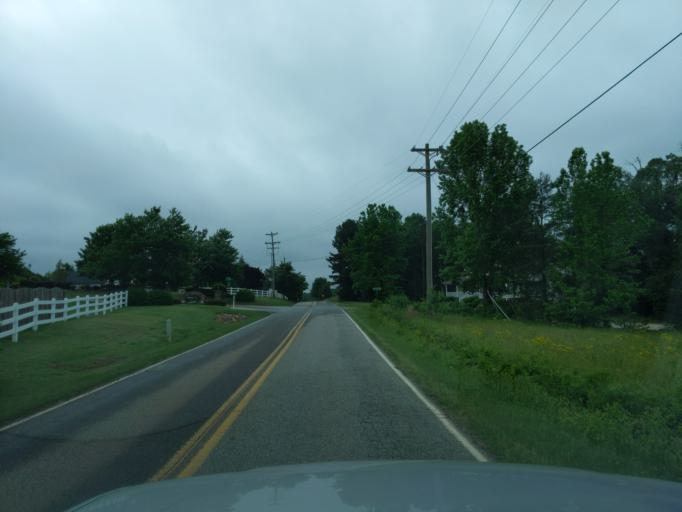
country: US
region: South Carolina
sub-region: Greenville County
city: Five Forks
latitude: 34.8565
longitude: -82.2153
